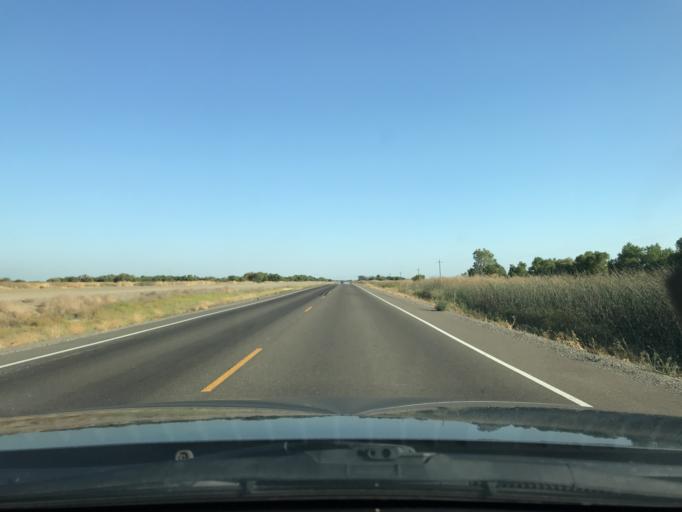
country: US
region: California
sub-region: Merced County
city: Los Banos
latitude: 37.1766
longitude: -120.8334
